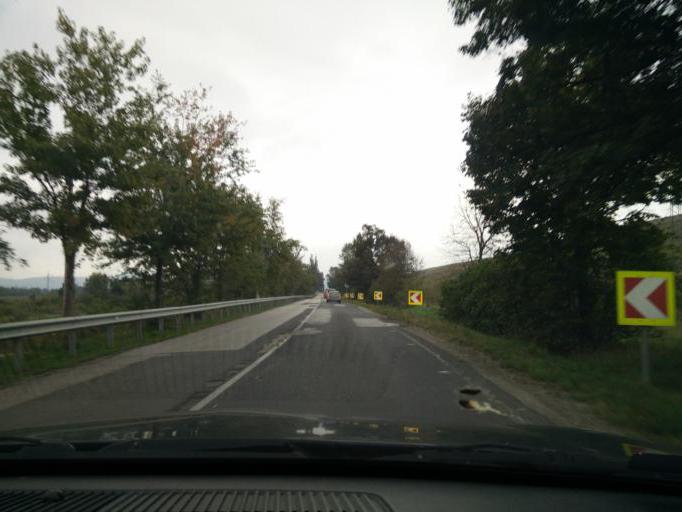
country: HU
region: Komarom-Esztergom
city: Dorog
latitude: 47.6941
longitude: 18.7626
